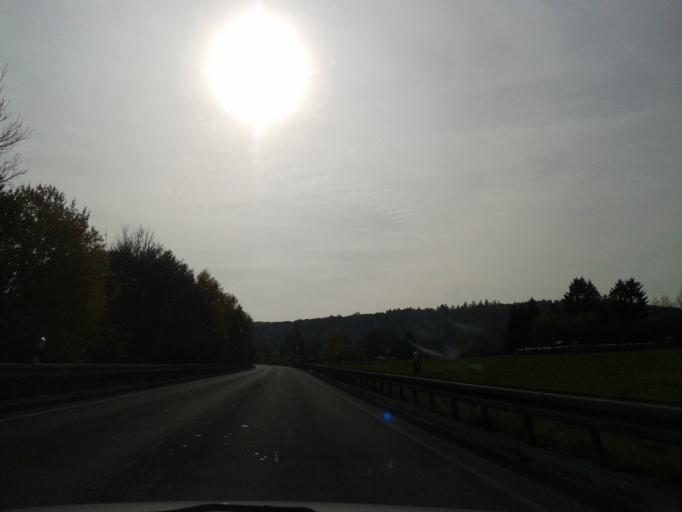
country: DE
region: North Rhine-Westphalia
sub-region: Regierungsbezirk Arnsberg
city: Ruthen
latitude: 51.4465
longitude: 8.4384
